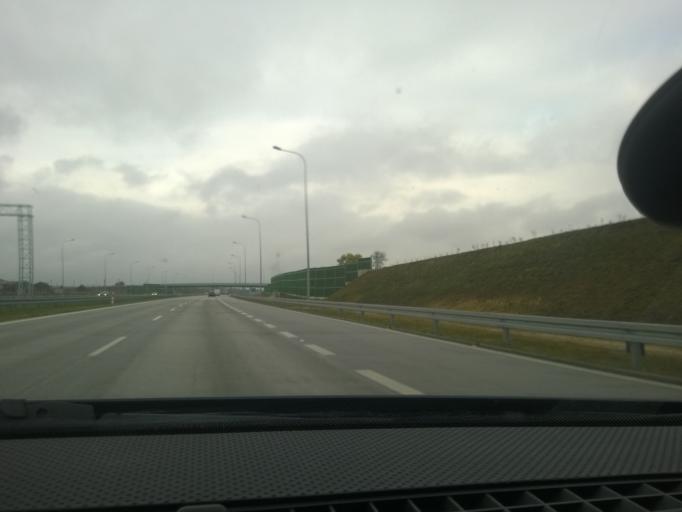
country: PL
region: Lodz Voivodeship
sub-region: Powiat lodzki wschodni
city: Andrespol
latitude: 51.8016
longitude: 19.6235
